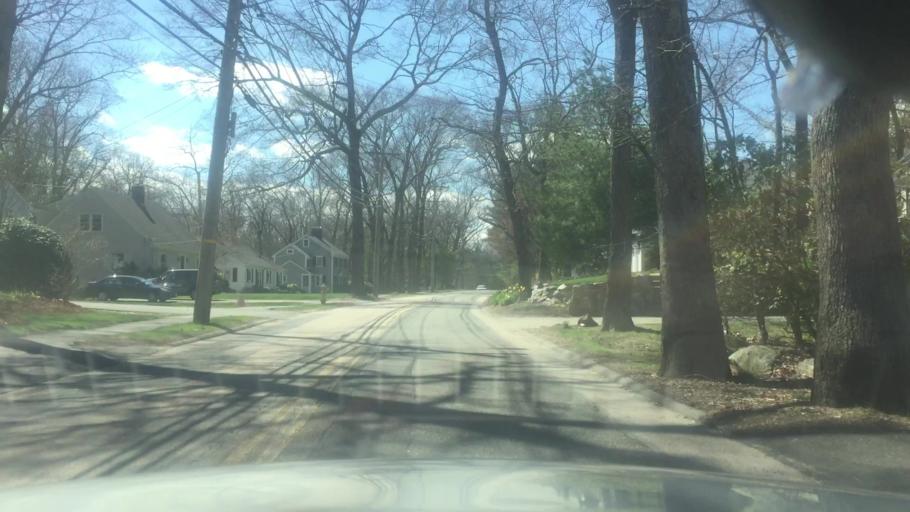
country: US
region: Massachusetts
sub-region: Norfolk County
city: Needham
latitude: 42.2758
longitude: -71.2525
